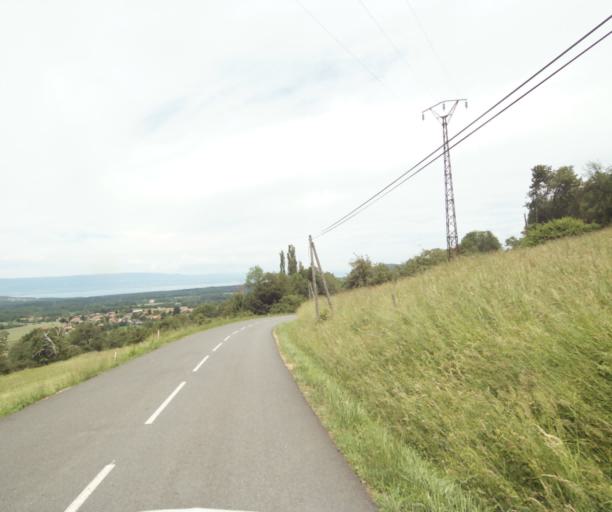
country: FR
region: Rhone-Alpes
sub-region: Departement de la Haute-Savoie
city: Bons-en-Chablais
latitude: 46.2679
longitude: 6.4117
